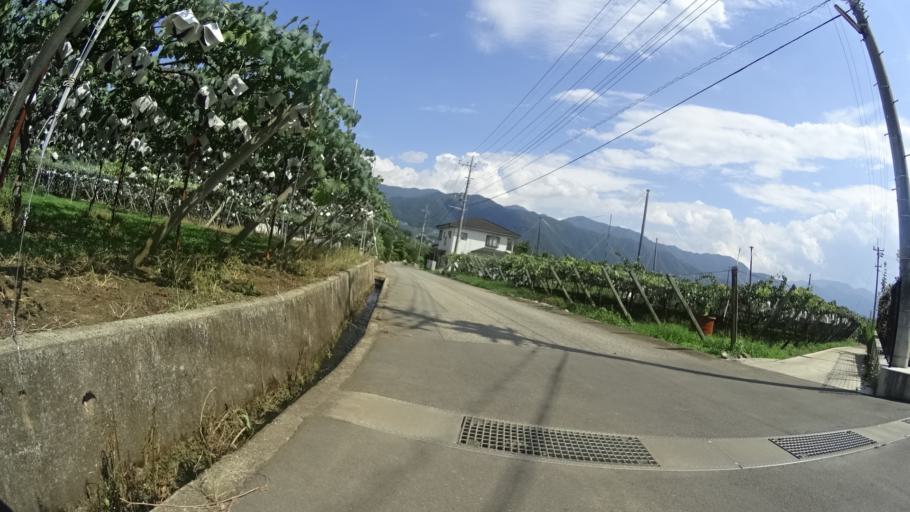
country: JP
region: Yamanashi
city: Enzan
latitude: 35.7229
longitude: 138.7282
